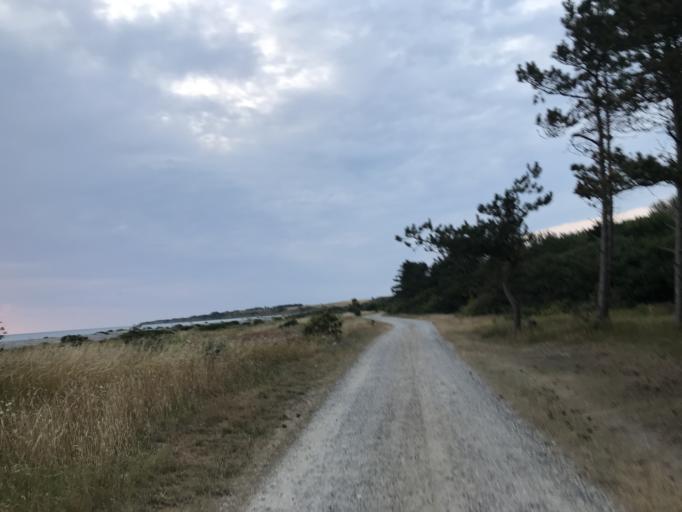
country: DK
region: South Denmark
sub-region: Faaborg-Midtfyn Kommune
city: Faaborg
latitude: 54.9333
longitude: 10.2447
